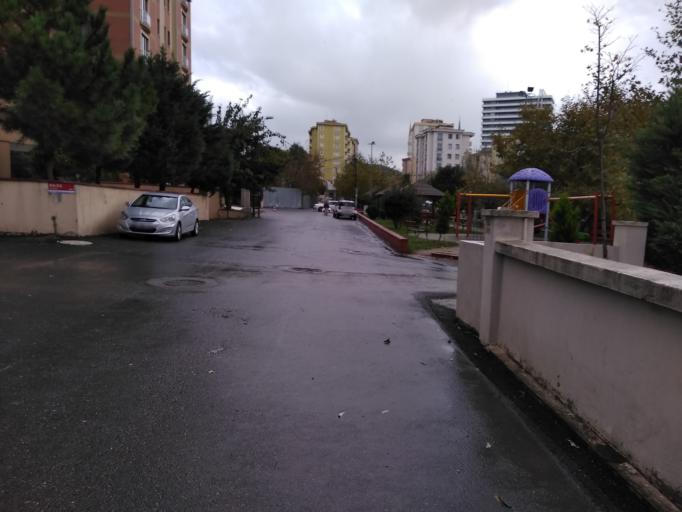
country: TR
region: Istanbul
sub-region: Atasehir
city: Atasehir
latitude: 40.9817
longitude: 29.1232
